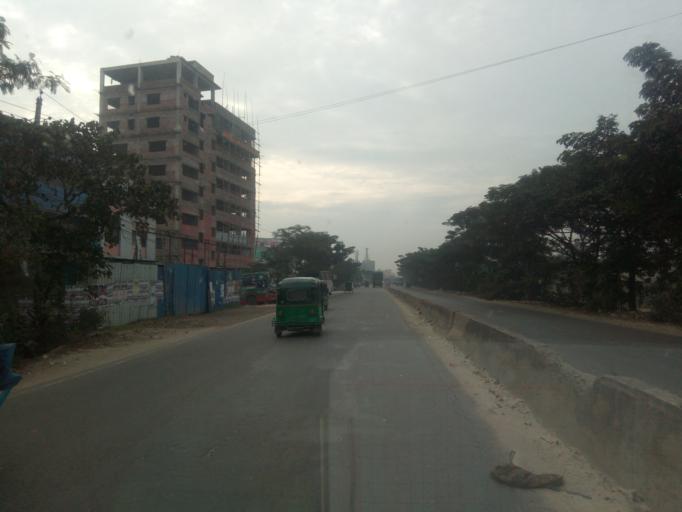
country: BD
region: Dhaka
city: Narayanganj
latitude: 23.6855
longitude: 90.4819
